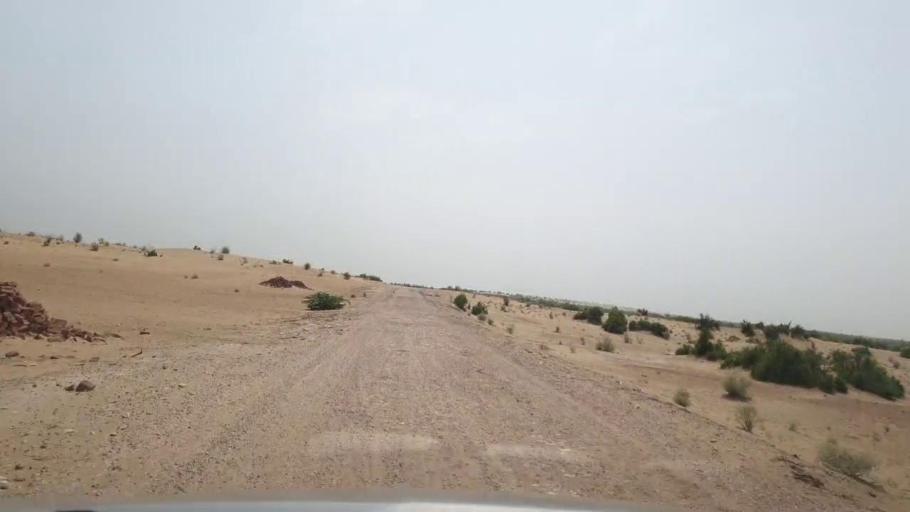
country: PK
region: Sindh
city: Pano Aqil
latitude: 27.6170
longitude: 69.1255
